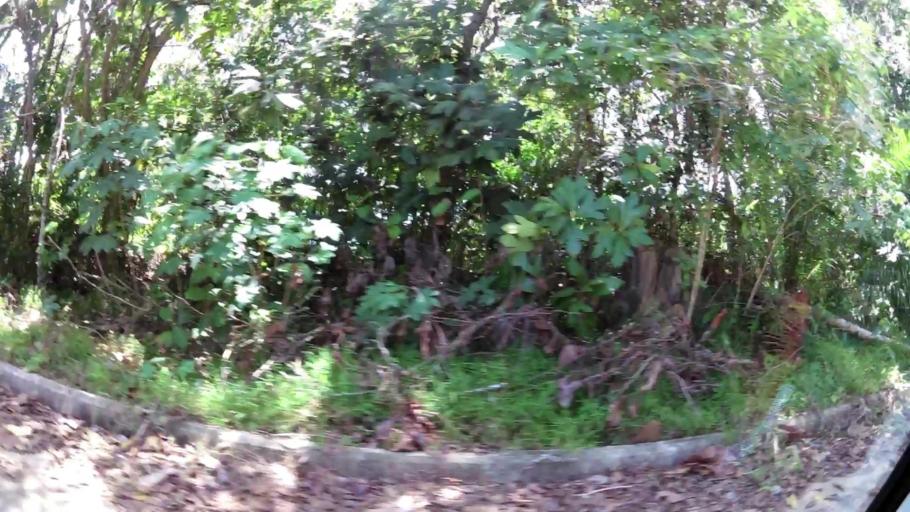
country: BN
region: Brunei and Muara
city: Bandar Seri Begawan
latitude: 4.9332
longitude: 114.9562
